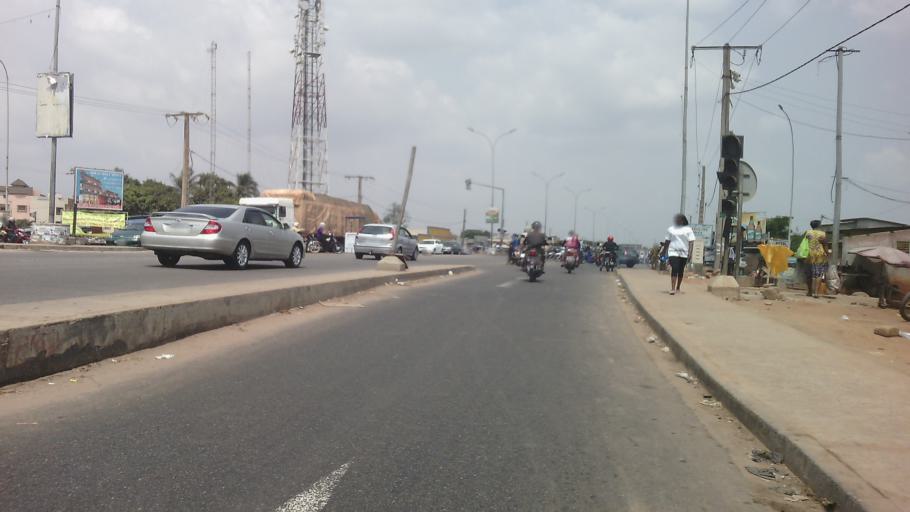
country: BJ
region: Atlantique
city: Abomey-Calavi
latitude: 6.4455
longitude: 2.3542
